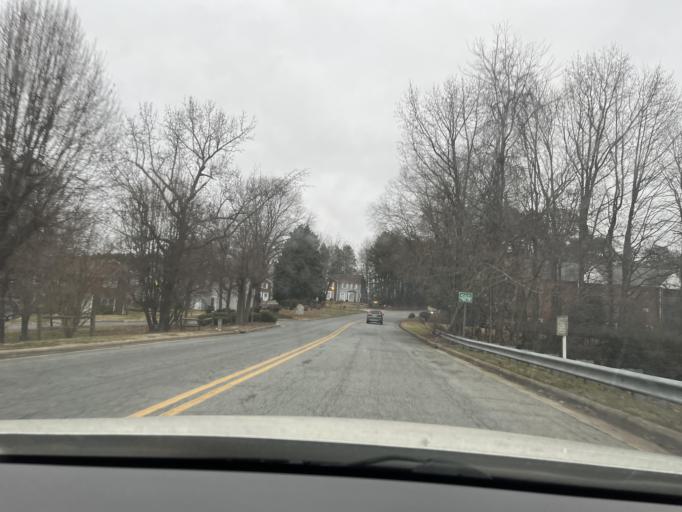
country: US
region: North Carolina
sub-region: Guilford County
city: Greensboro
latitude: 36.0224
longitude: -79.7861
